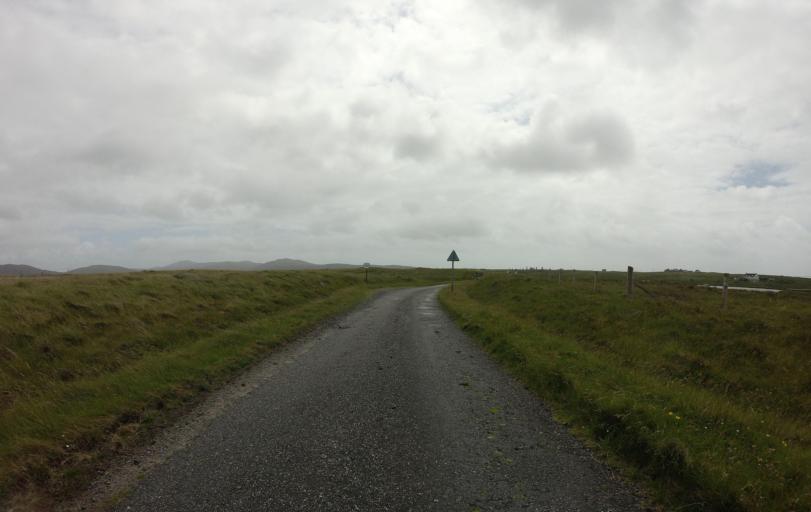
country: GB
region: Scotland
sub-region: Eilean Siar
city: Isle of South Uist
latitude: 57.2677
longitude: -7.3984
